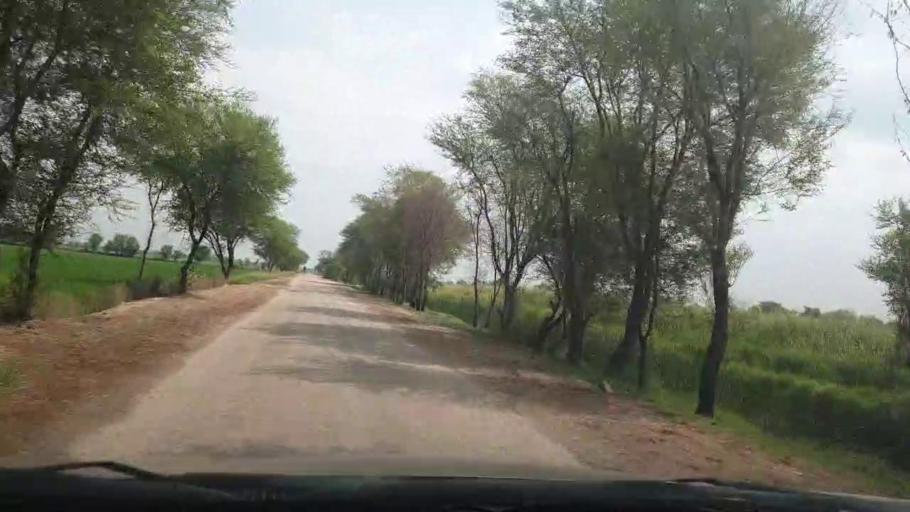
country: PK
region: Sindh
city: Miro Khan
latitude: 27.6930
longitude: 68.1972
